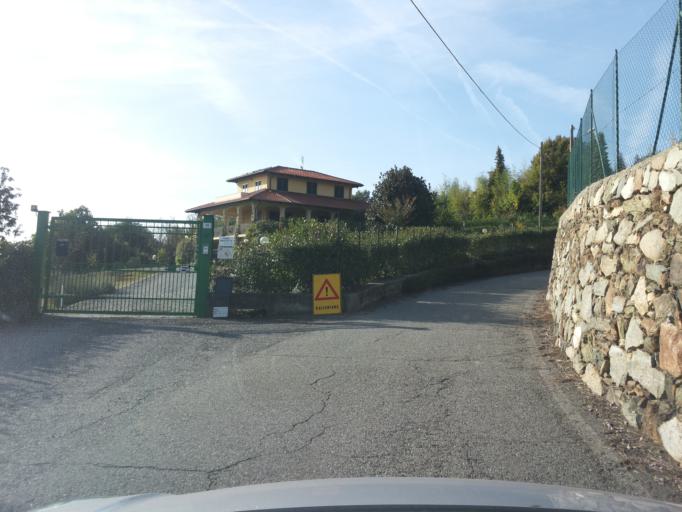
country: IT
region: Piedmont
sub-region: Provincia di Biella
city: Roppolo
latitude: 45.4257
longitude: 8.0727
